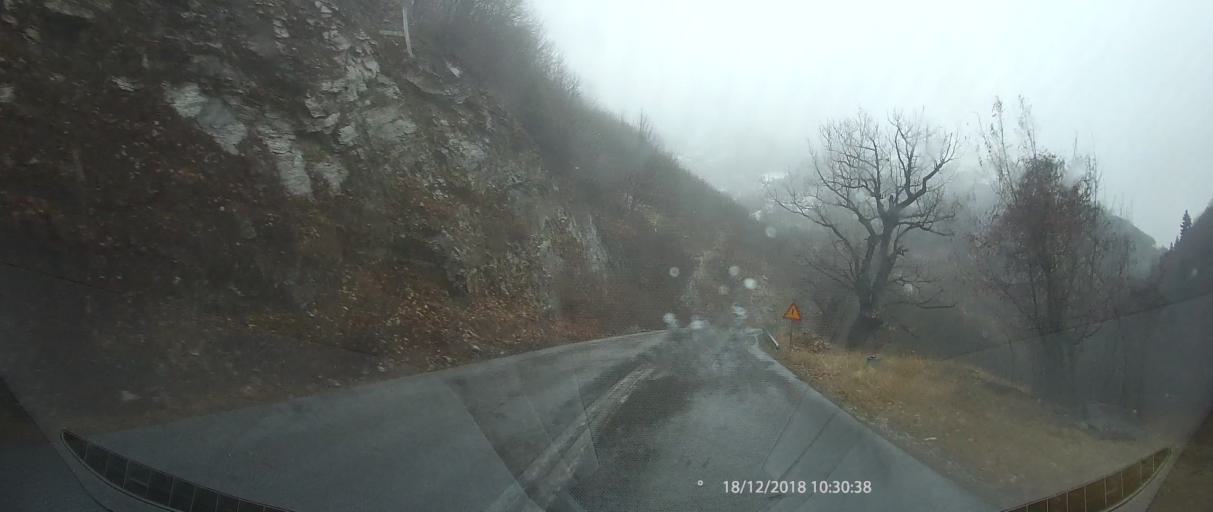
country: GR
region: Central Macedonia
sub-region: Nomos Pierias
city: Kato Milia
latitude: 40.1893
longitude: 22.2781
